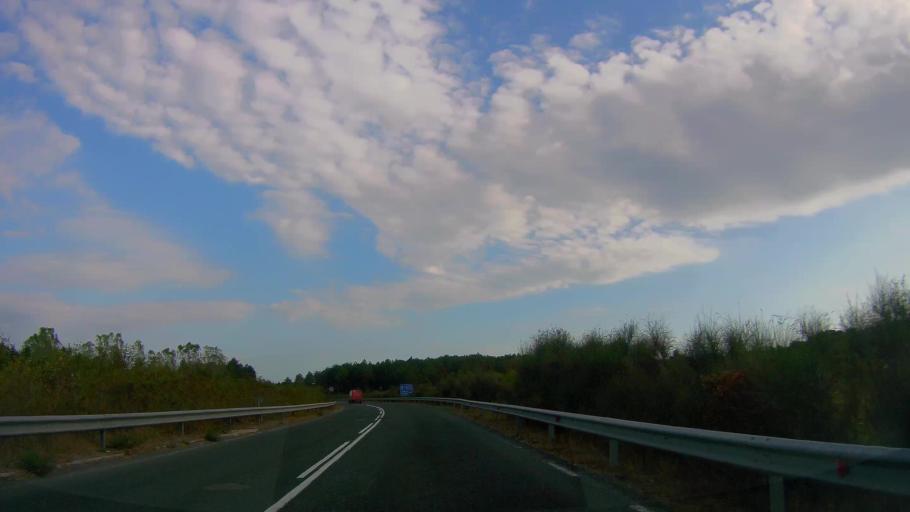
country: BG
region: Burgas
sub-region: Obshtina Sozopol
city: Sozopol
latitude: 42.4024
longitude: 27.6758
